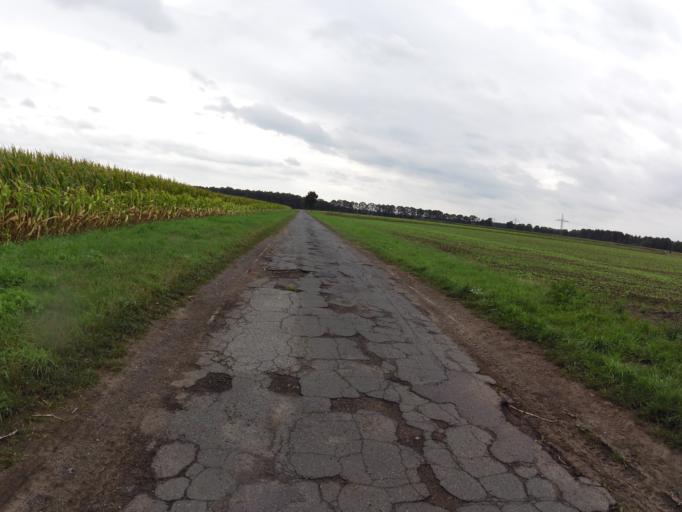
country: DE
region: Lower Saxony
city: Scheessel
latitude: 53.1539
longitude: 9.4539
